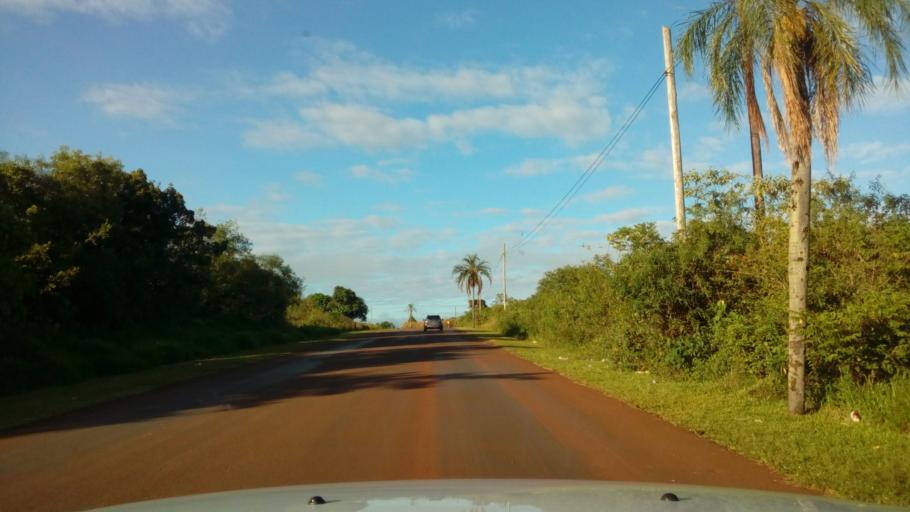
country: AR
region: Misiones
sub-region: Departamento de San Javier
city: San Javier
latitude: -27.8882
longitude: -55.1339
